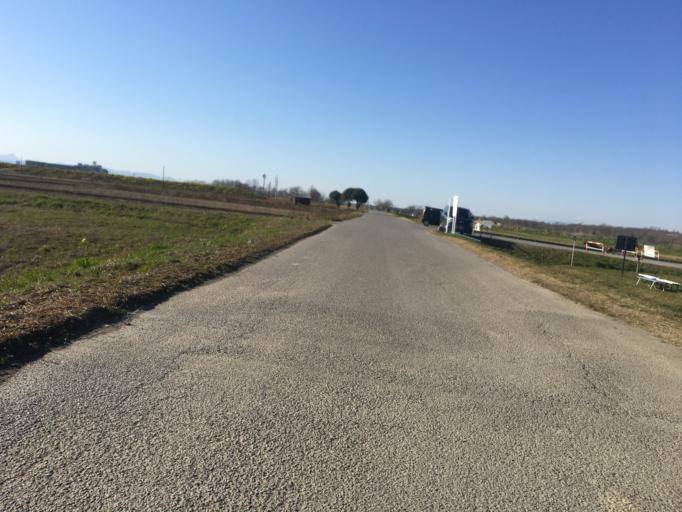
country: JP
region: Saitama
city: Shiki
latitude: 35.8427
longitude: 139.6009
